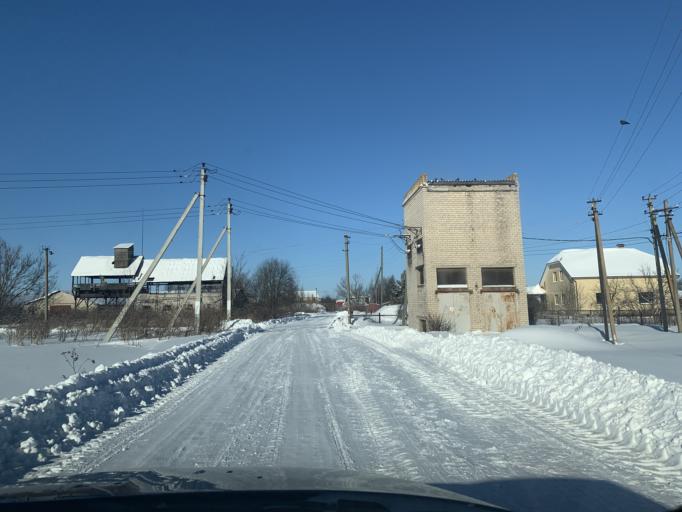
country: RU
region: Jaroslavl
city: Tunoshna
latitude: 57.6605
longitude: 40.0679
